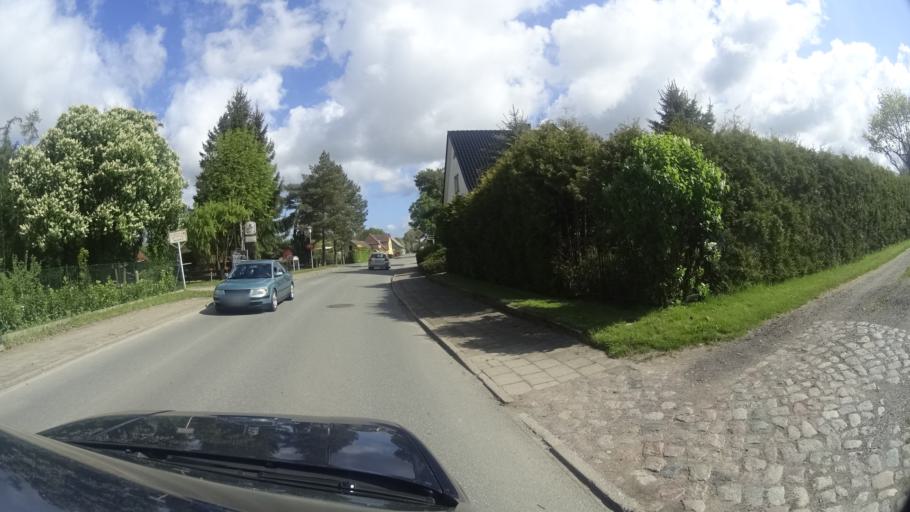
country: DE
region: Mecklenburg-Vorpommern
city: Trinwillershagen
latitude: 54.3016
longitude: 12.5826
